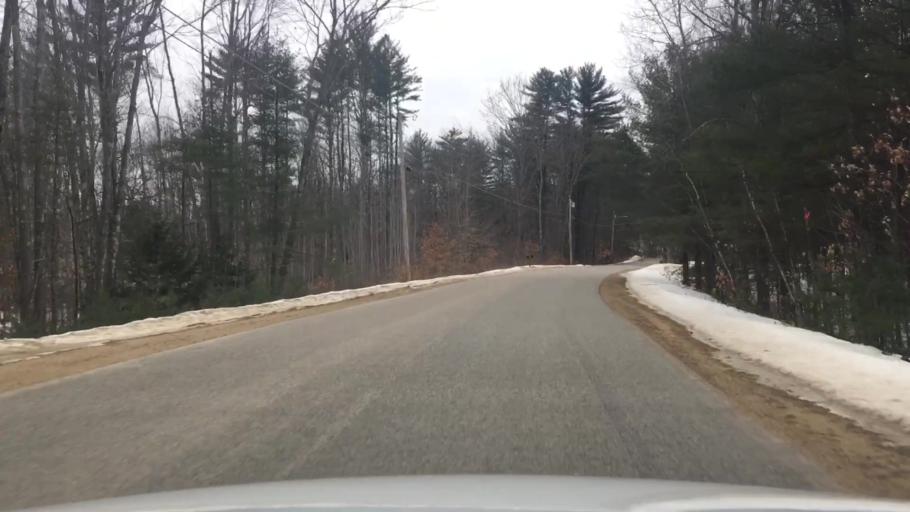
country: US
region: New Hampshire
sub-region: Strafford County
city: Rochester
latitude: 43.3642
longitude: -70.9714
